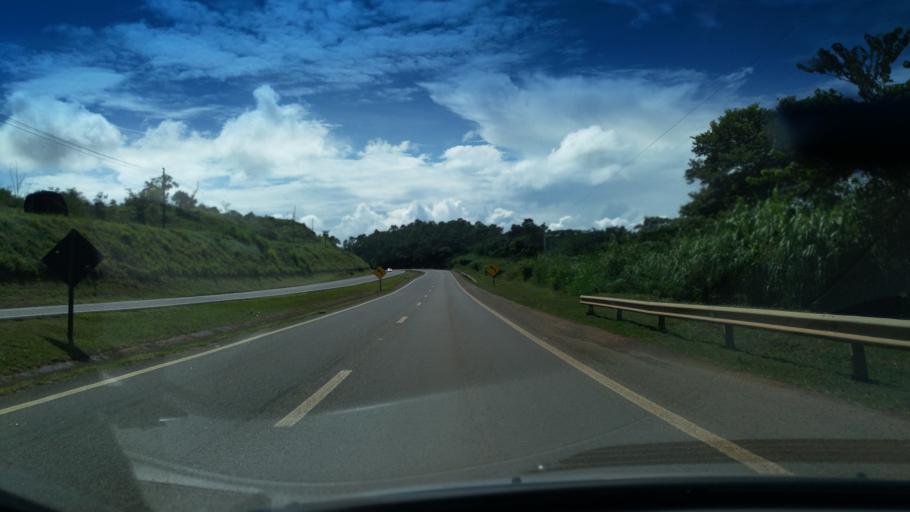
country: BR
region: Sao Paulo
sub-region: Santo Antonio Do Jardim
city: Espirito Santo do Pinhal
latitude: -22.2213
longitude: -46.7900
